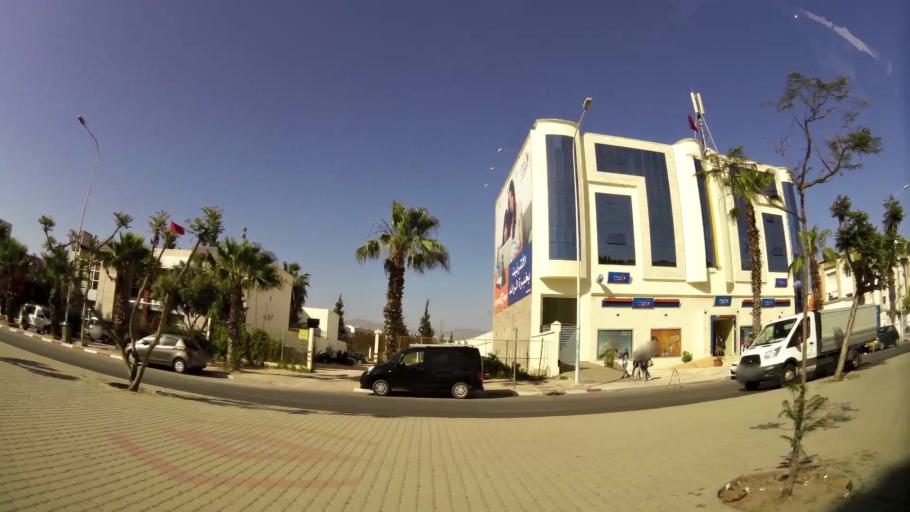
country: MA
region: Oued ed Dahab-Lagouira
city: Dakhla
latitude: 30.4130
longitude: -9.5661
